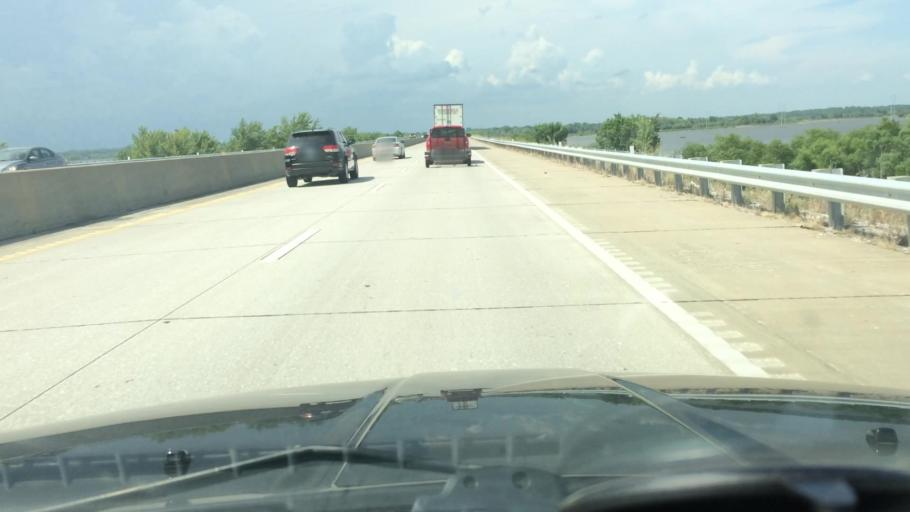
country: US
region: Missouri
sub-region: Henry County
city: Clinton
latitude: 38.3148
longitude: -93.7581
